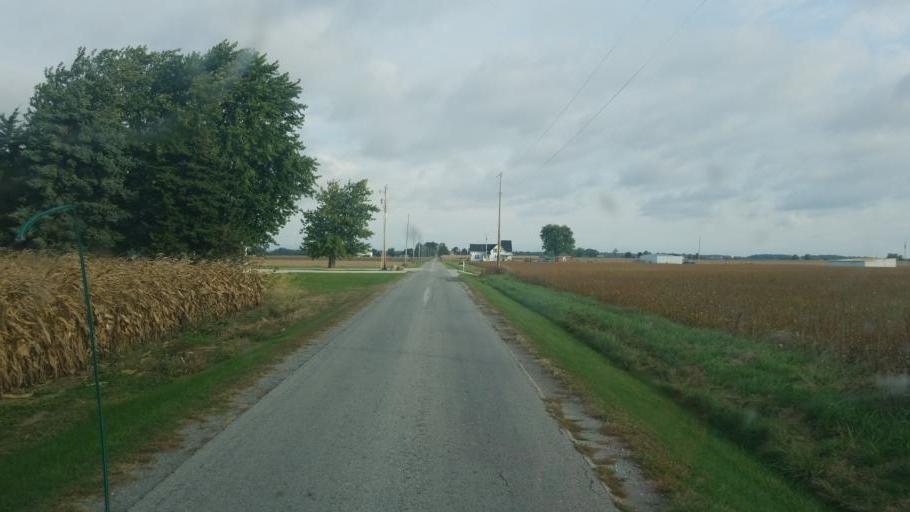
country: US
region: Ohio
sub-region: Wyandot County
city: Carey
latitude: 41.0001
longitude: -83.4301
